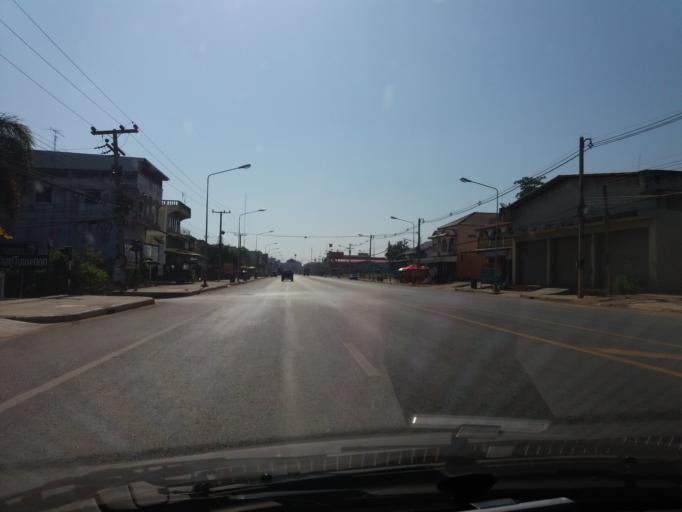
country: TH
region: Kamphaeng Phet
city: Khlong Khlung
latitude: 16.2400
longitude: 99.7275
